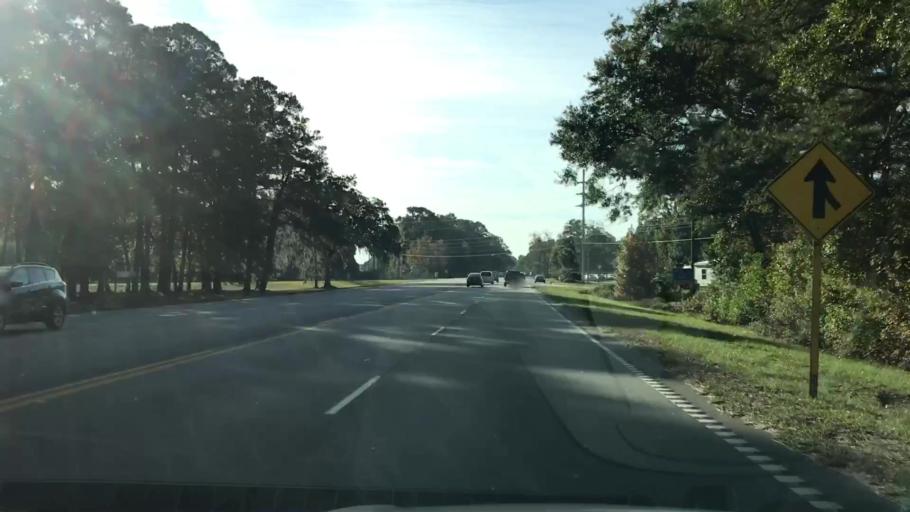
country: US
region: South Carolina
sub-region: Beaufort County
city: Burton
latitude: 32.4567
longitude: -80.7334
